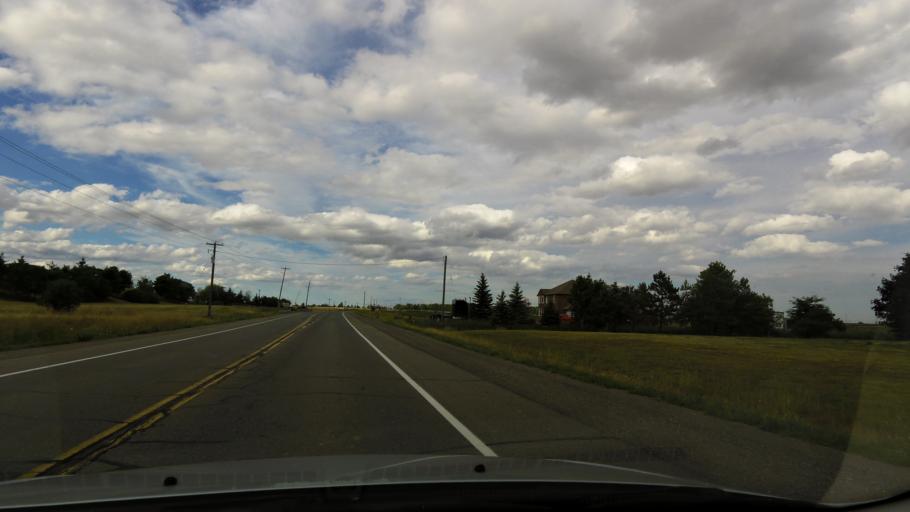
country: CA
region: Ontario
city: Brampton
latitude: 43.6896
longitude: -79.8721
